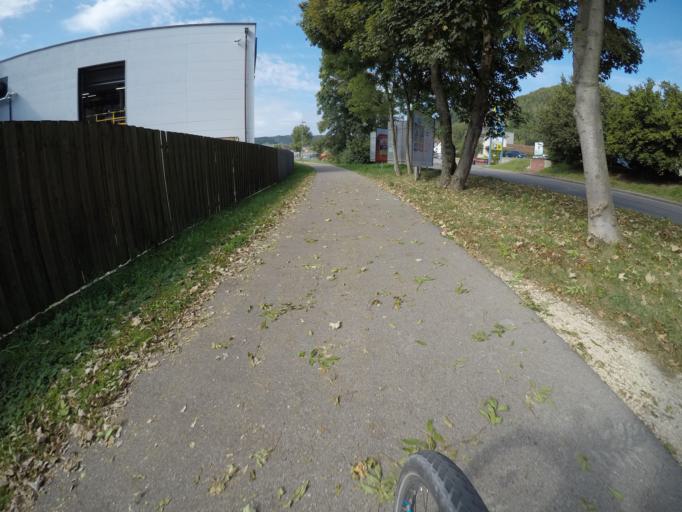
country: DE
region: Baden-Wuerttemberg
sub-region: Regierungsbezirk Stuttgart
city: Geislingen an der Steige
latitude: 48.6294
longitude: 9.8446
